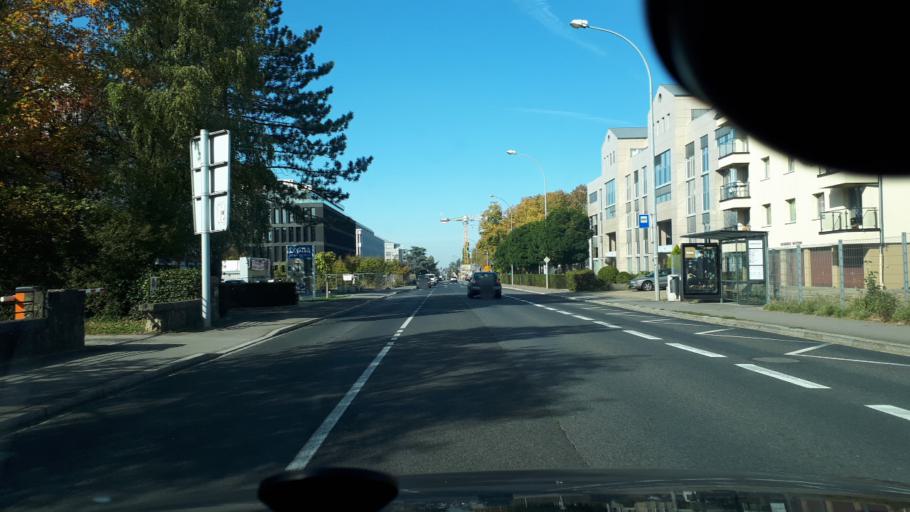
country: LU
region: Luxembourg
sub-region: Canton de Luxembourg
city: Luxembourg
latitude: 49.6159
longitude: 6.1026
